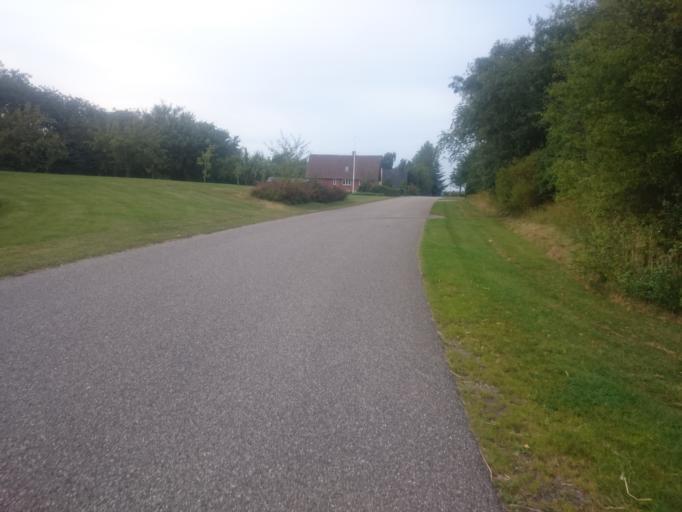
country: DK
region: South Denmark
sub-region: Billund Kommune
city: Billund
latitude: 55.7319
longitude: 9.0757
